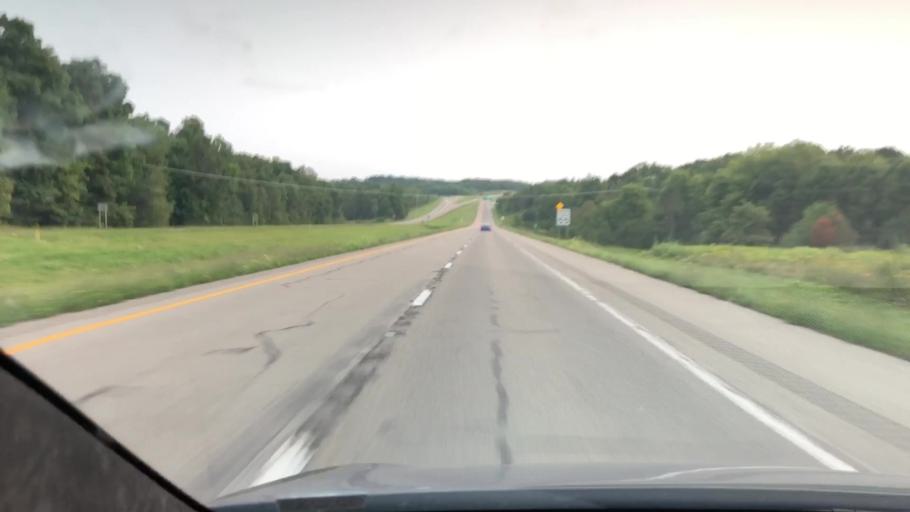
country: US
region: Pennsylvania
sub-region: Mercer County
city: Grove City
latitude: 41.2409
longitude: -79.9493
